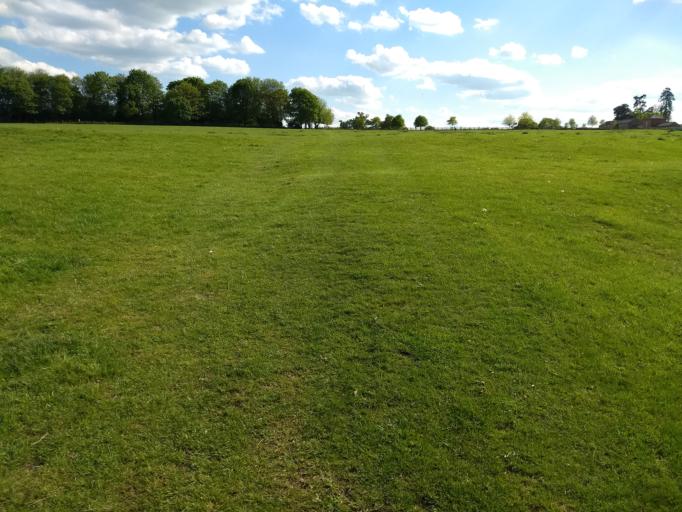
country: GB
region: England
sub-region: Milton Keynes
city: Castlethorpe
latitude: 52.0703
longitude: -0.8204
